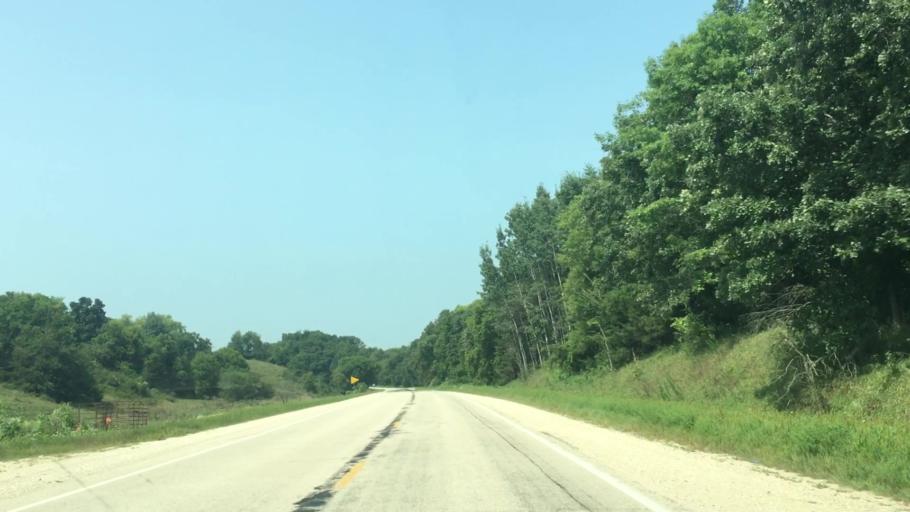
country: US
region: Iowa
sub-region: Fayette County
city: West Union
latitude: 43.0733
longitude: -91.8390
